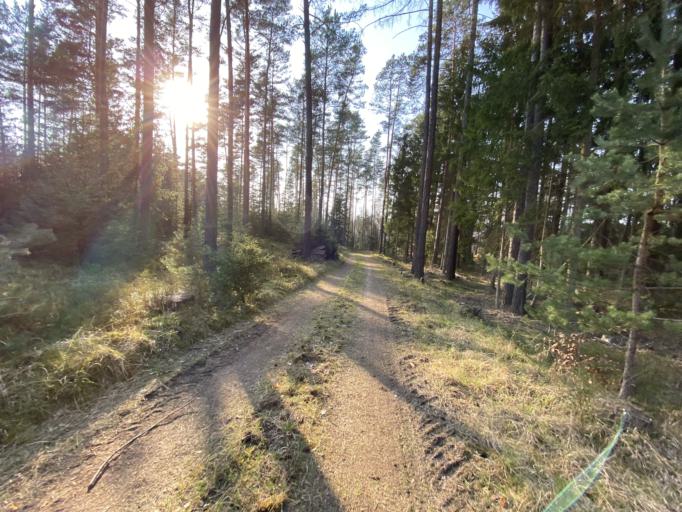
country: DE
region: Bavaria
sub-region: Regierungsbezirk Mittelfranken
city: Buckenhof
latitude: 49.5532
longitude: 11.0661
